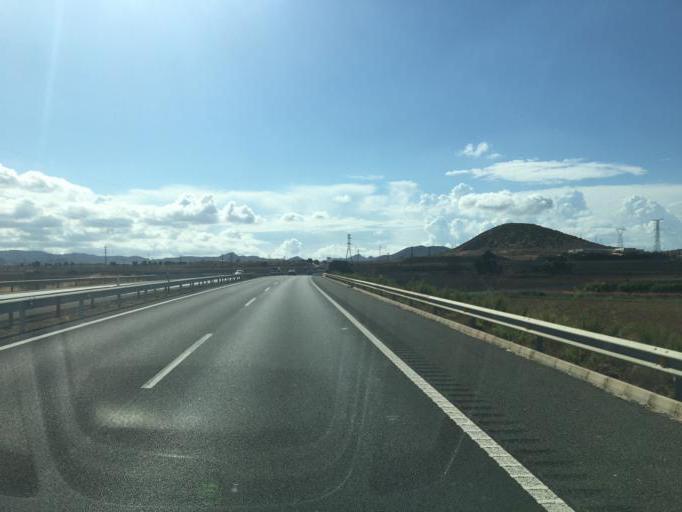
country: ES
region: Murcia
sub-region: Murcia
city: Cartagena
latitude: 37.6401
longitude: -0.9617
